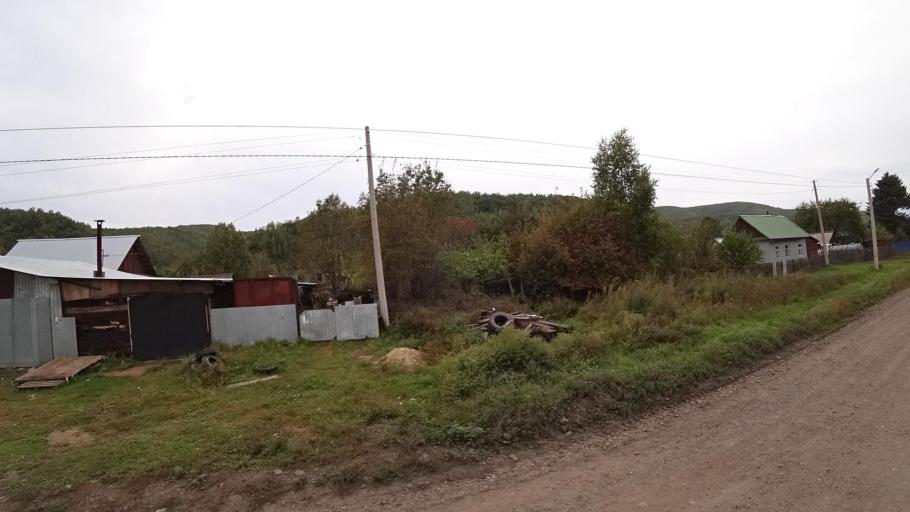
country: RU
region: Jewish Autonomous Oblast
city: Khingansk
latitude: 49.0258
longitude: 131.0480
